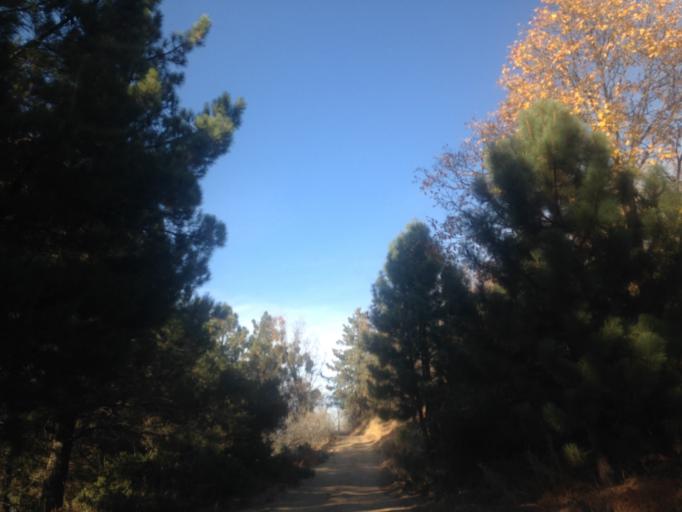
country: US
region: California
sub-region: San Bernardino County
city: Yucaipa
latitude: 34.1357
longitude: -117.0105
